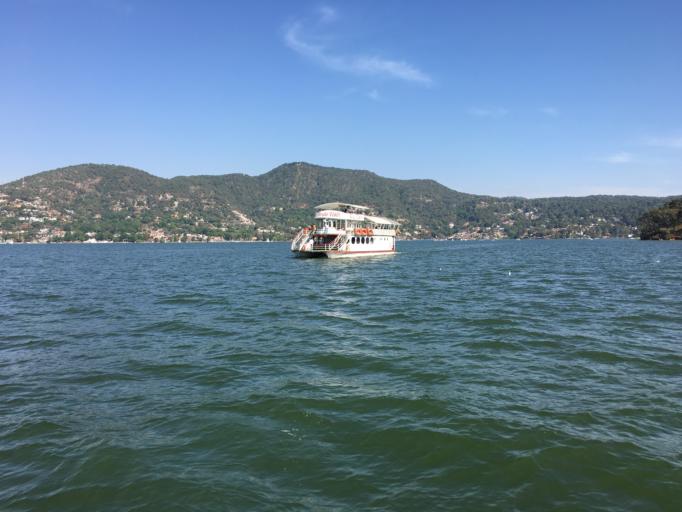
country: MX
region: Mexico
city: Valle de Bravo
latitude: 19.1798
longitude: -100.1446
